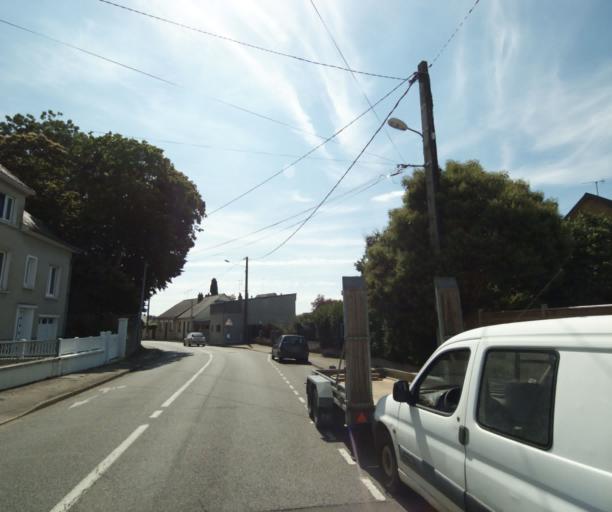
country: FR
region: Pays de la Loire
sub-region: Departement de la Mayenne
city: Laval
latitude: 48.0604
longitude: -0.7675
